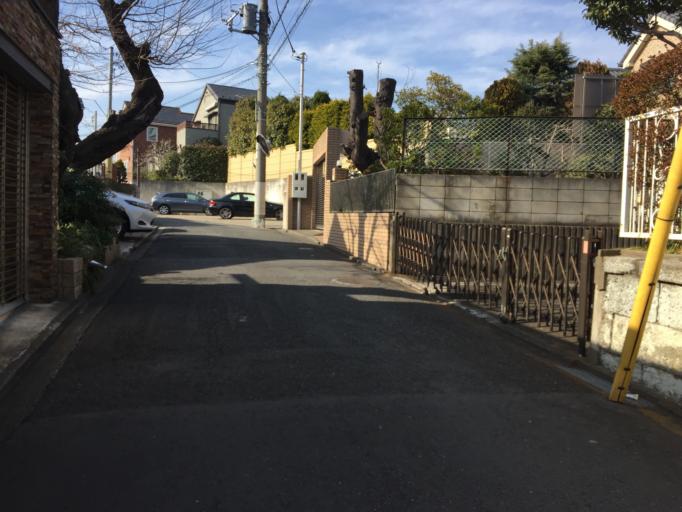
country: JP
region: Kanagawa
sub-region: Kawasaki-shi
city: Kawasaki
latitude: 35.5940
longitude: 139.6627
